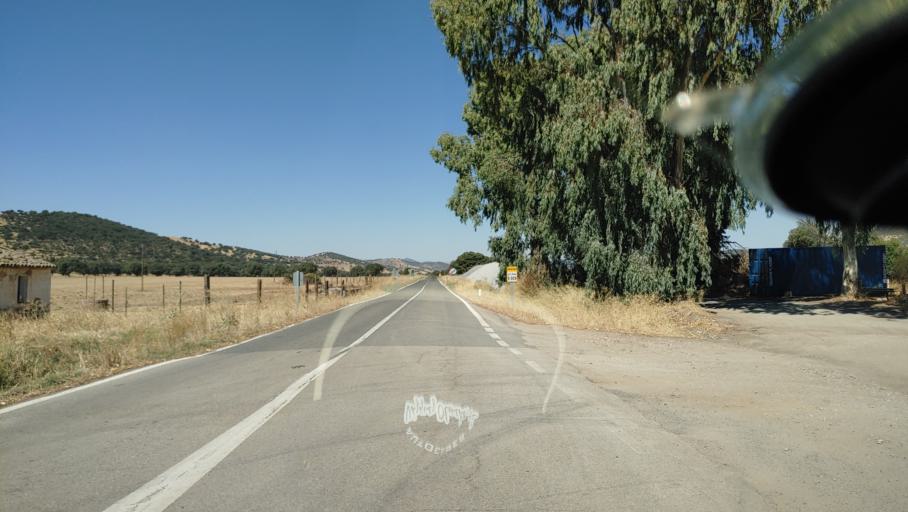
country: ES
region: Castille-La Mancha
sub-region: Provincia de Ciudad Real
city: Guadalmez
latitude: 38.6992
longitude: -4.9302
